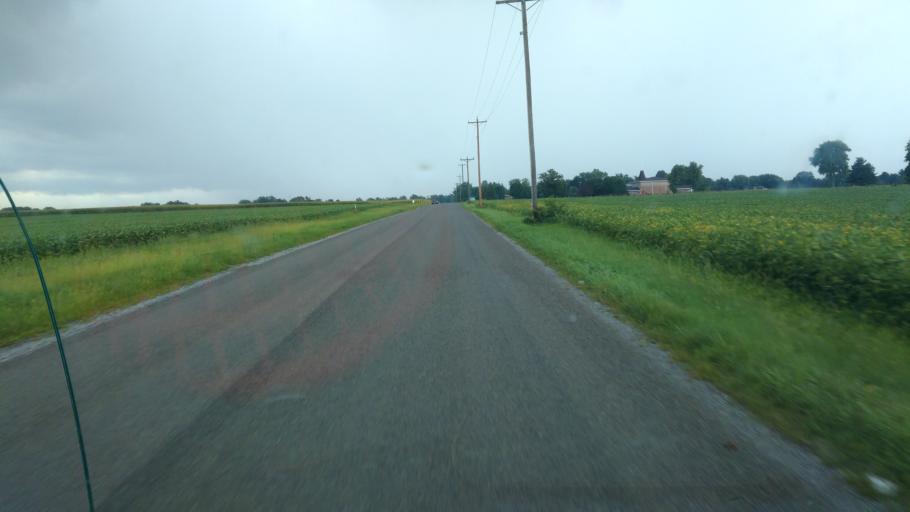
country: US
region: Ohio
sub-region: Hardin County
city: Kenton
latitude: 40.6541
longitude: -83.5761
